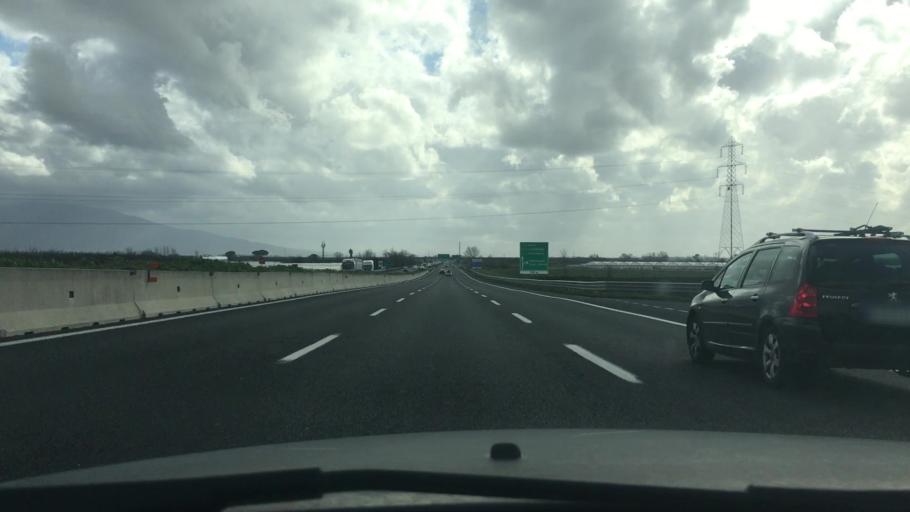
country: IT
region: Campania
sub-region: Provincia di Napoli
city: Pascarola
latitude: 40.9839
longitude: 14.3253
